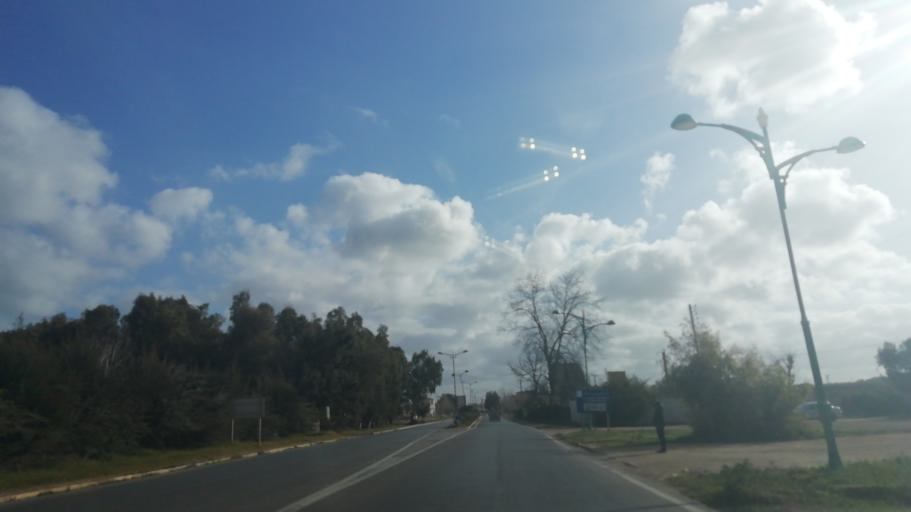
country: DZ
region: Relizane
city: Mazouna
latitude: 36.2522
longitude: 0.5651
